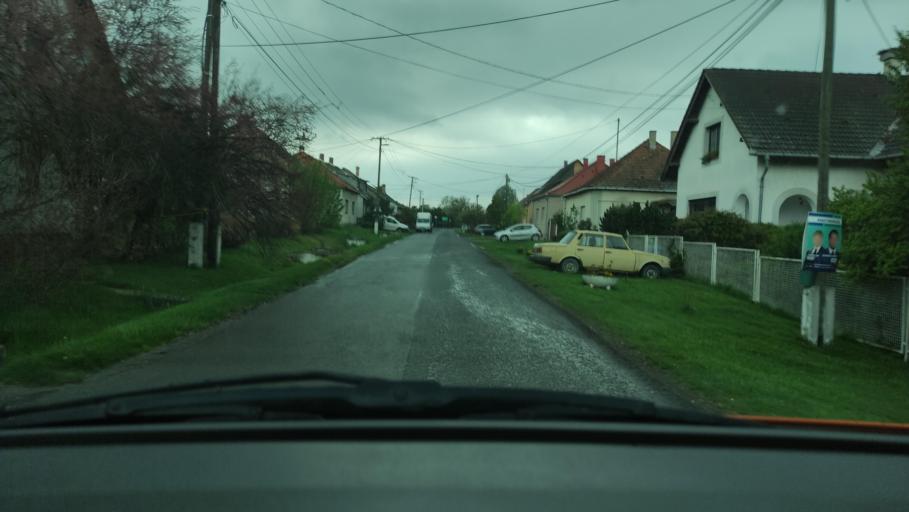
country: HU
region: Baranya
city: Mohacs
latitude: 45.9459
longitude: 18.7025
